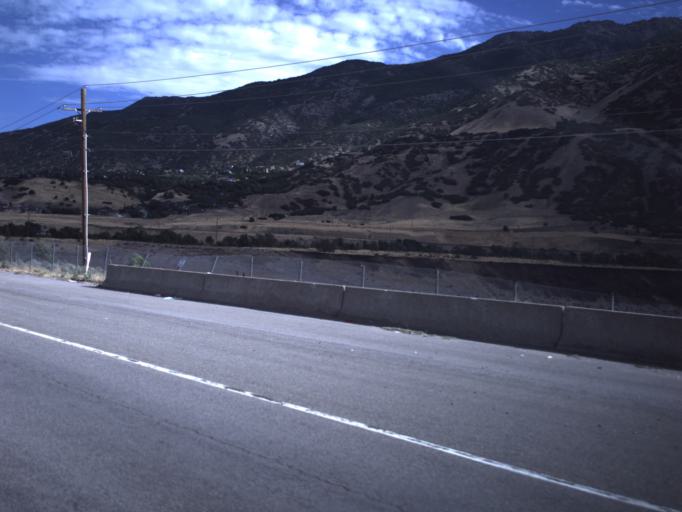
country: US
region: Utah
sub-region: Weber County
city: Uintah
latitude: 41.1300
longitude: -111.9089
